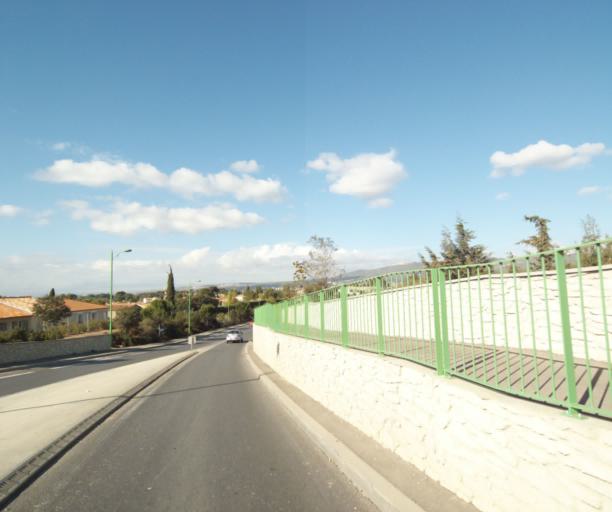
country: FR
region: Provence-Alpes-Cote d'Azur
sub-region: Departement des Bouches-du-Rhone
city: Allauch
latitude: 43.3358
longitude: 5.4763
